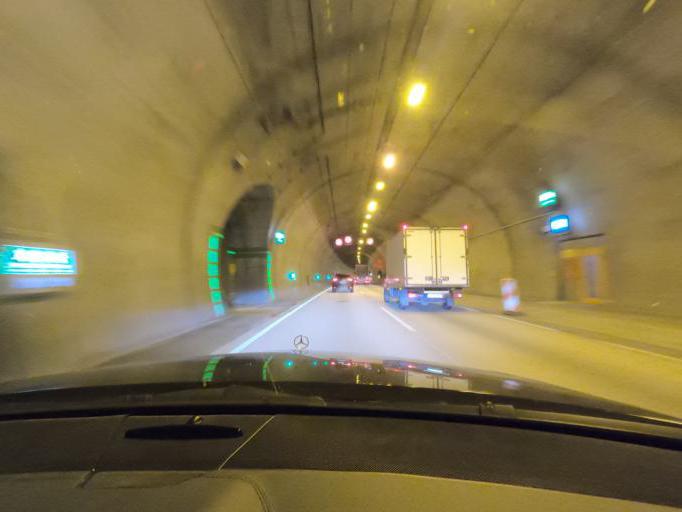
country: DE
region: Thuringia
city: Rustenfelde
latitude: 51.4091
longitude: 9.9844
